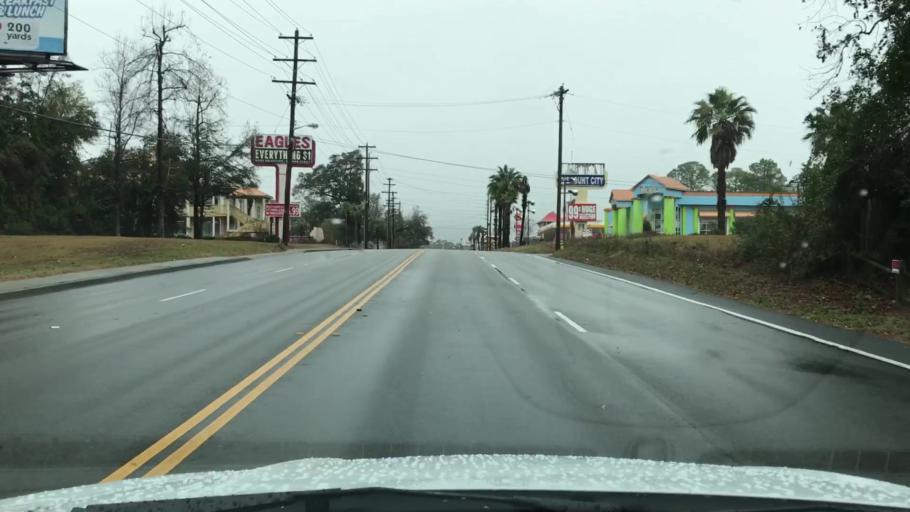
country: US
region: South Carolina
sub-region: Horry County
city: North Myrtle Beach
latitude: 33.7741
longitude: -78.7901
